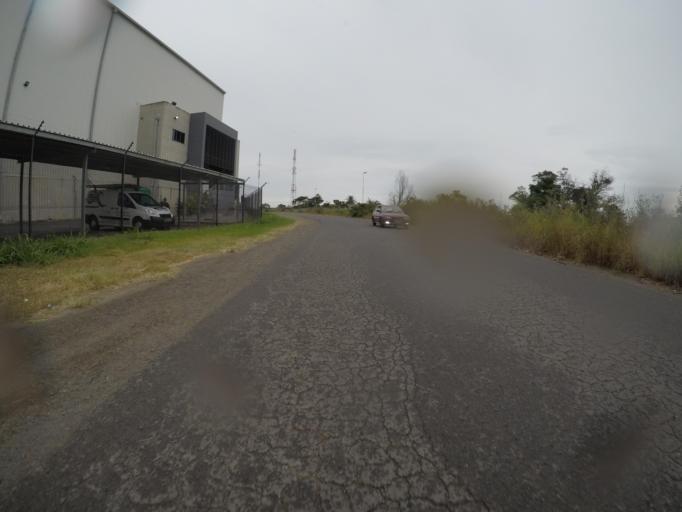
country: ZA
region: Eastern Cape
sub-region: Buffalo City Metropolitan Municipality
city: East London
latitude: -32.9754
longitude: 27.8180
